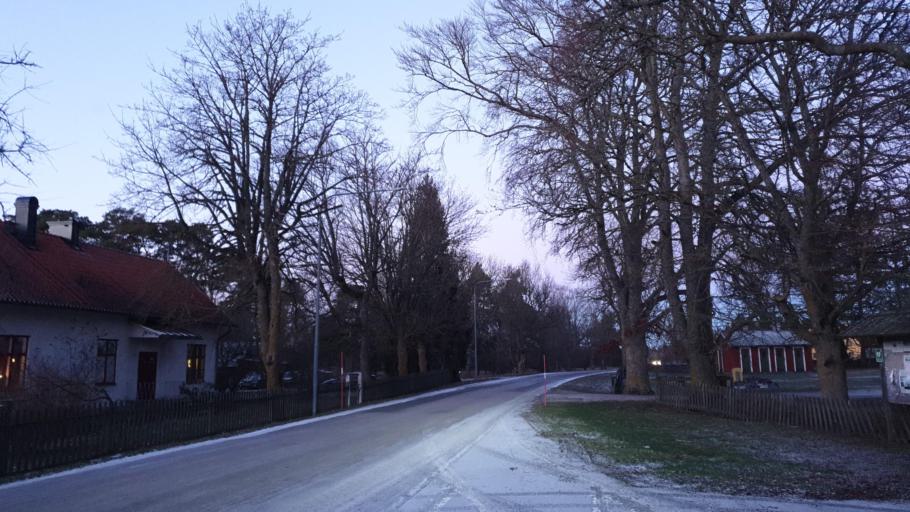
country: SE
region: Gotland
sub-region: Gotland
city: Slite
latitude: 57.4047
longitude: 18.8041
